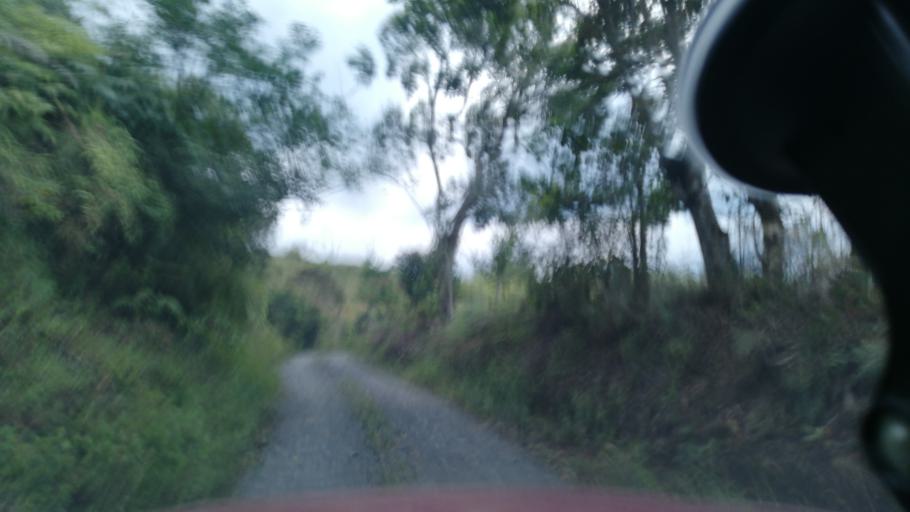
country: CO
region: Cundinamarca
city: Vergara
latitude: 5.1843
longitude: -74.2721
